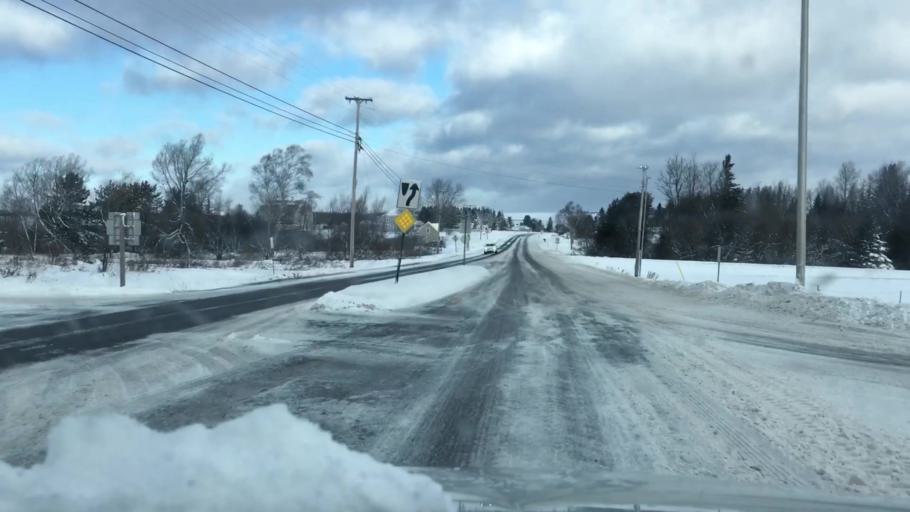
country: US
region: Maine
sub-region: Aroostook County
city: Caribou
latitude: 46.8880
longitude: -68.0142
